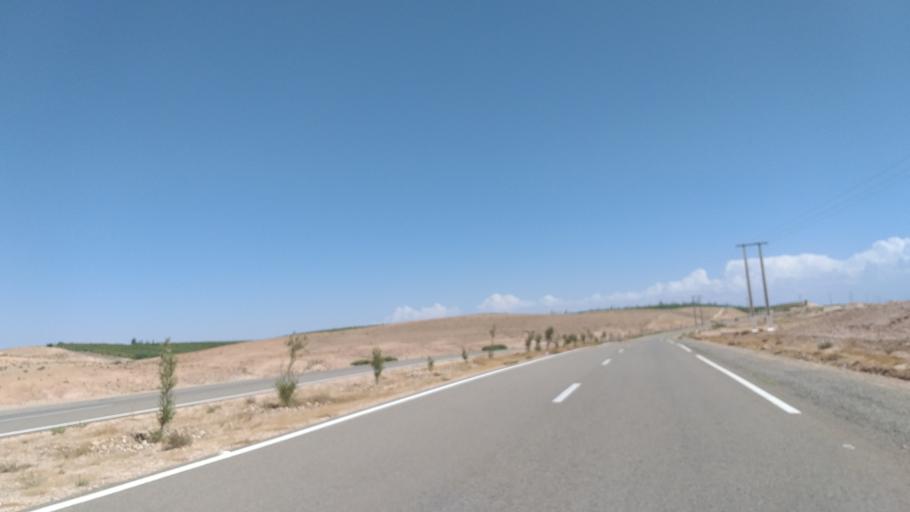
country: MA
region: Marrakech-Tensift-Al Haouz
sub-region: Chichaoua
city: Chichaoua
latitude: 31.4977
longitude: -8.7169
